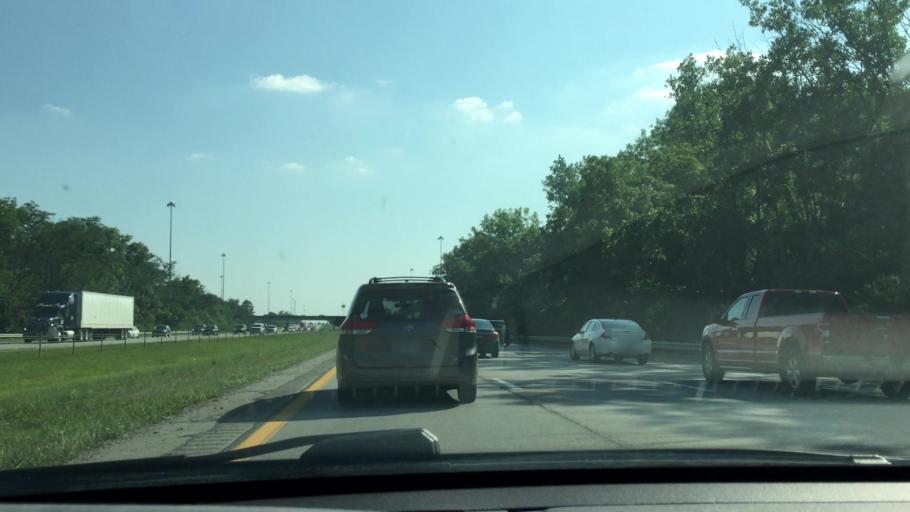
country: US
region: Ohio
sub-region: Franklin County
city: Blacklick Estates
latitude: 39.9086
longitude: -82.8920
